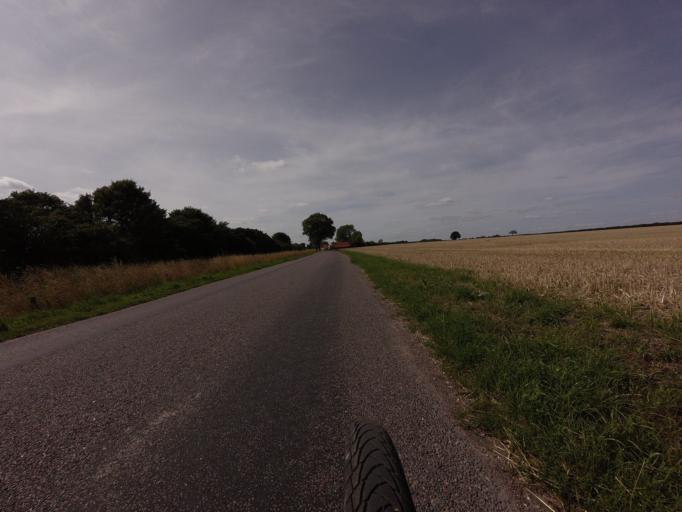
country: DK
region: Zealand
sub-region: Stevns Kommune
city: Store Heddinge
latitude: 55.2424
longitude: 12.3278
